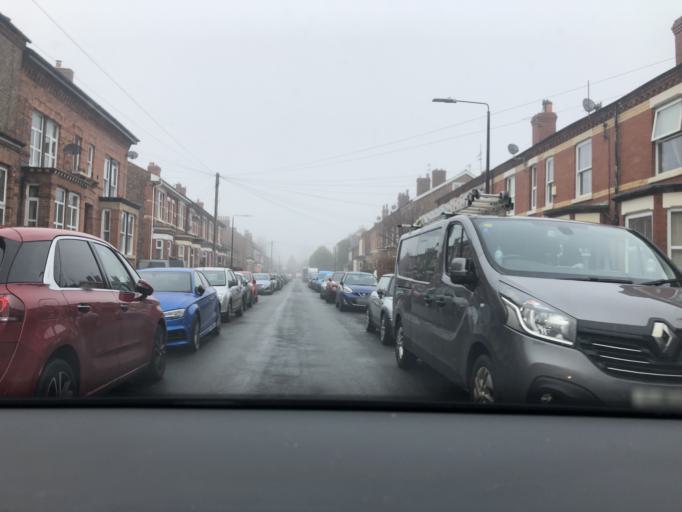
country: GB
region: England
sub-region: Trafford
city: Urmston
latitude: 53.4503
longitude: -2.3581
